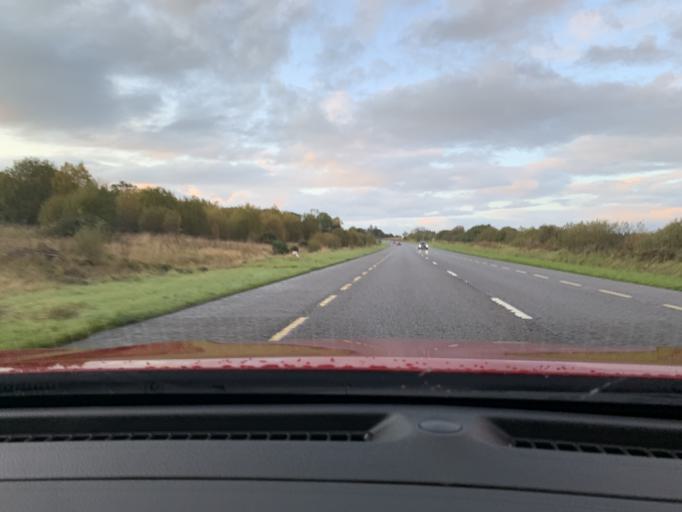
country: IE
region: Connaught
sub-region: Roscommon
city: Boyle
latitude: 54.0487
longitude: -8.3395
